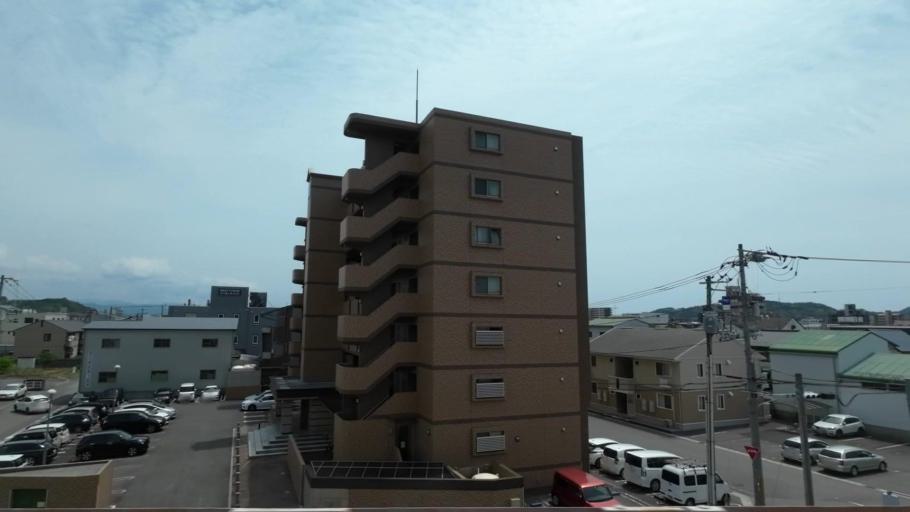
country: JP
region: Kochi
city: Kochi-shi
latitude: 33.5713
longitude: 133.5536
